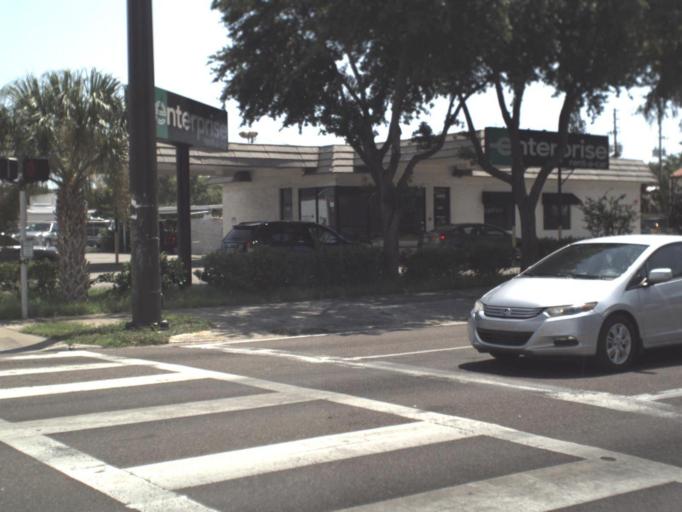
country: US
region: Florida
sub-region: Pinellas County
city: Saint Petersburg
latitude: 27.7665
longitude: -82.6795
